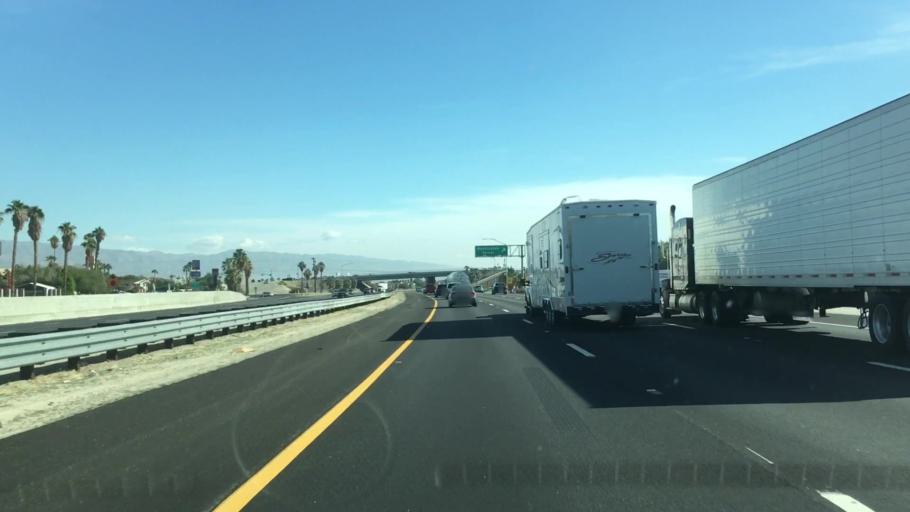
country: US
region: California
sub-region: Riverside County
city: Bermuda Dunes
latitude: 33.7615
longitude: -116.3069
